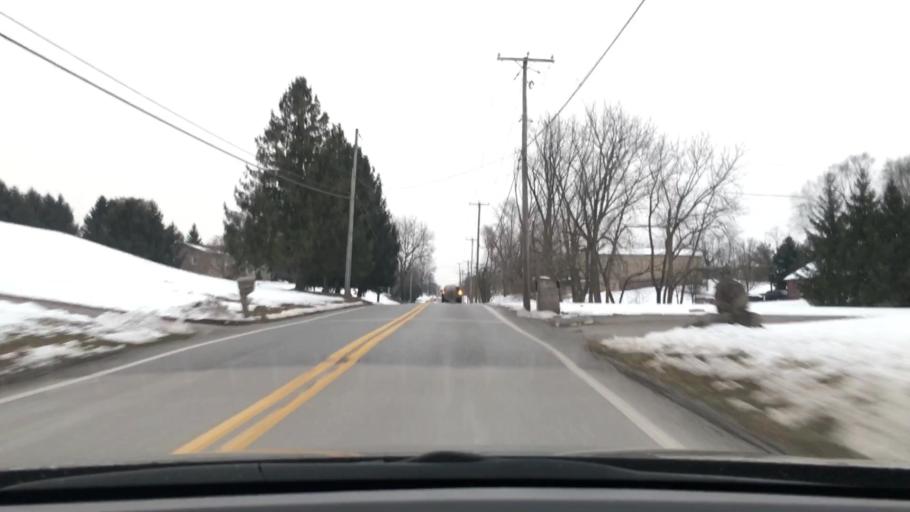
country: US
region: Pennsylvania
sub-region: York County
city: Weigelstown
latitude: 39.9579
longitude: -76.8354
